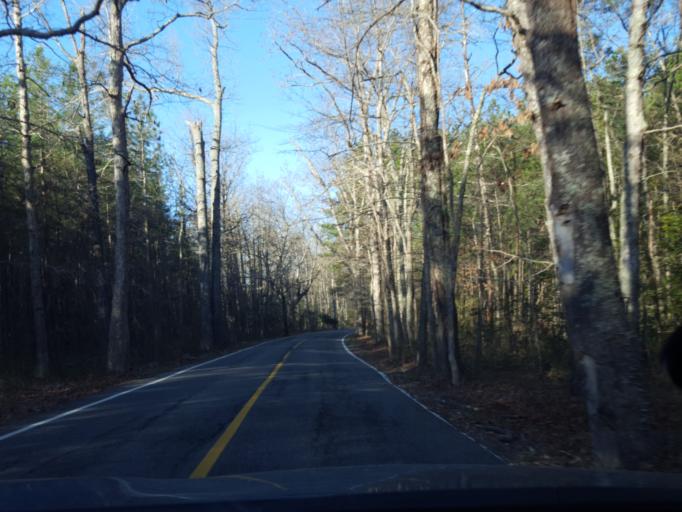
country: US
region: Maryland
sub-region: Prince George's County
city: Brandywine
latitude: 38.6592
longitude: -76.8317
